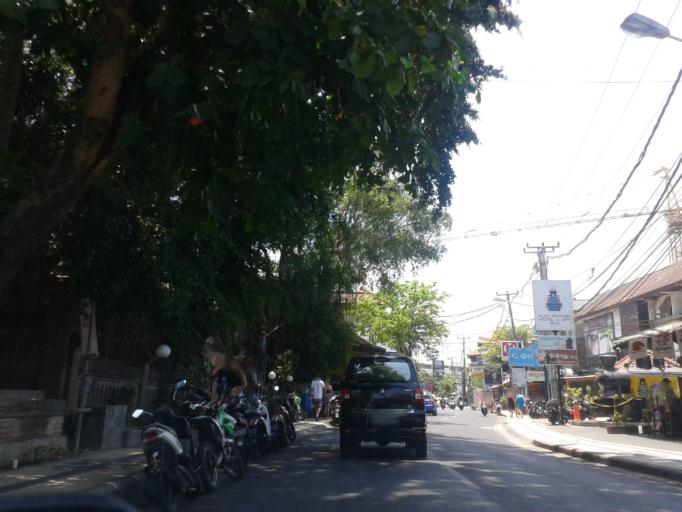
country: ID
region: Bali
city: Kuta
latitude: -8.7274
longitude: 115.1698
